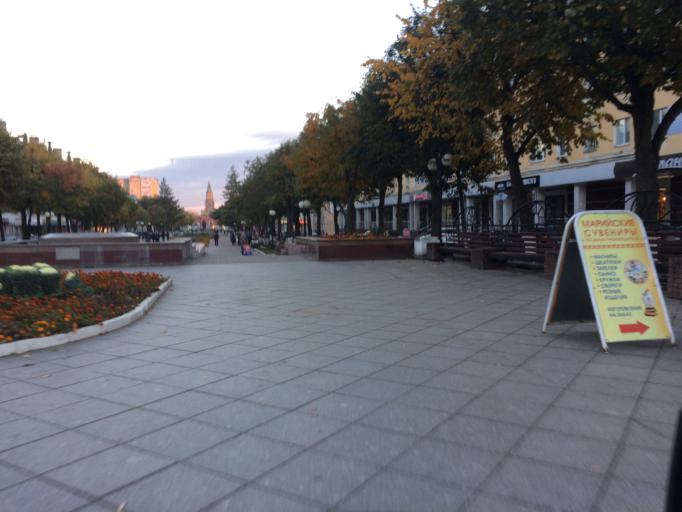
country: RU
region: Mariy-El
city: Yoshkar-Ola
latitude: 56.6357
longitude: 47.8934
